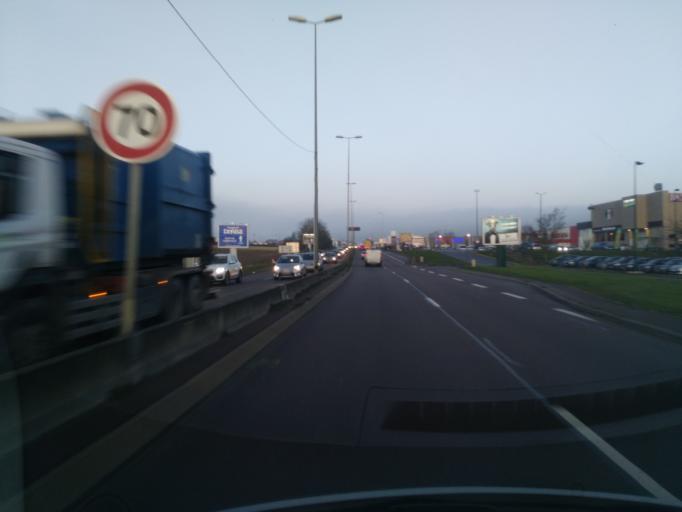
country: FR
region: Ile-de-France
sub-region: Departement des Yvelines
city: Orgeval
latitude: 48.9254
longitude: 1.9914
